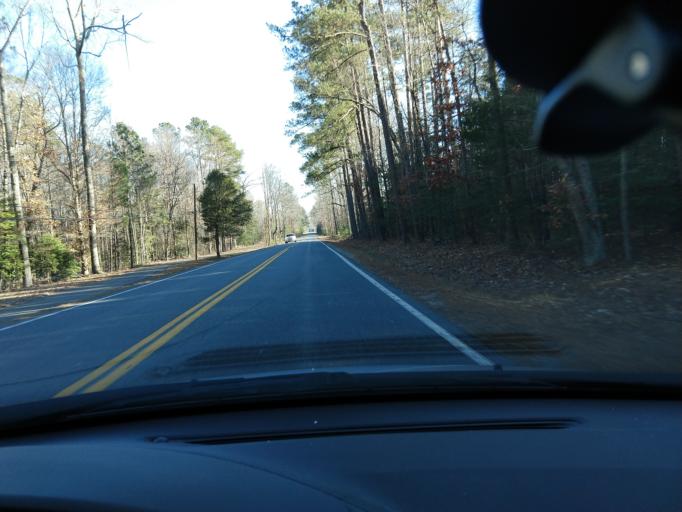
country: US
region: Virginia
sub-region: Charles City County
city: Charles City
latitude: 37.2906
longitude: -76.9315
